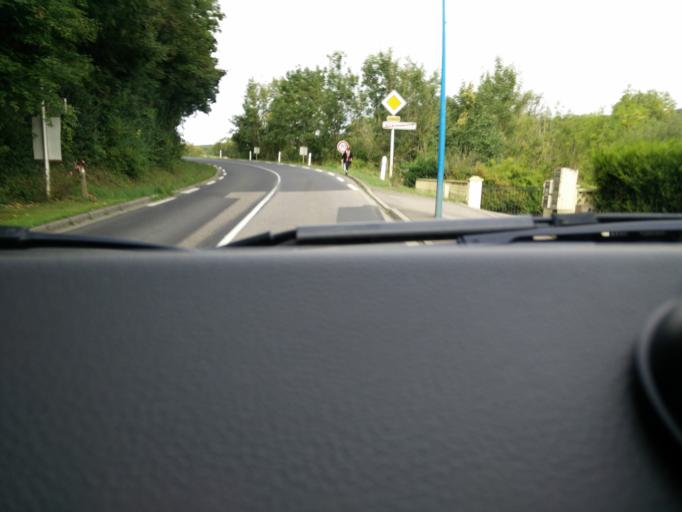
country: FR
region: Lorraine
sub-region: Departement de Meurthe-et-Moselle
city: Montauville
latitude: 48.9007
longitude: 6.0149
